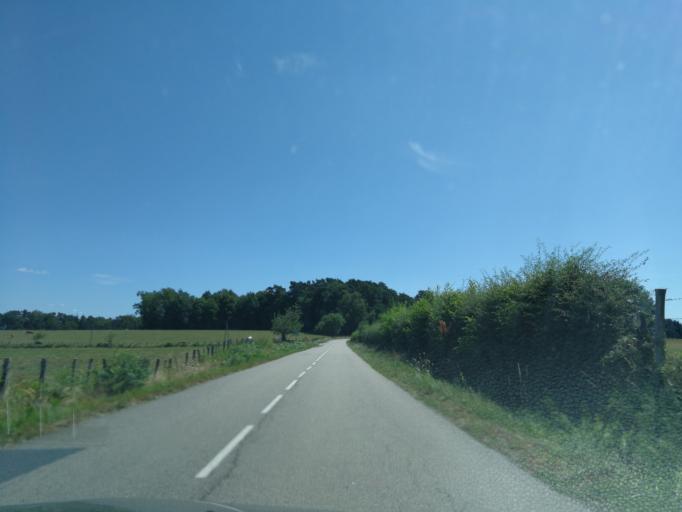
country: FR
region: Limousin
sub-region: Departement de la Correze
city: Argentat
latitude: 45.0330
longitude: 1.9589
